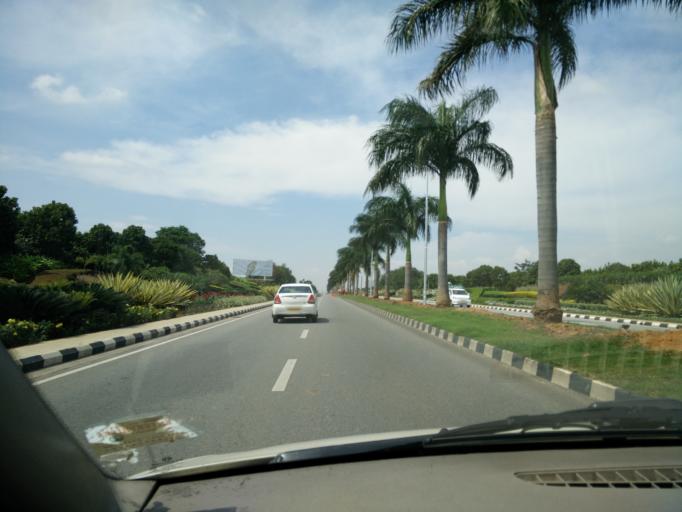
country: IN
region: Karnataka
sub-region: Bangalore Rural
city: Devanhalli
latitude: 13.1980
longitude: 77.6938
